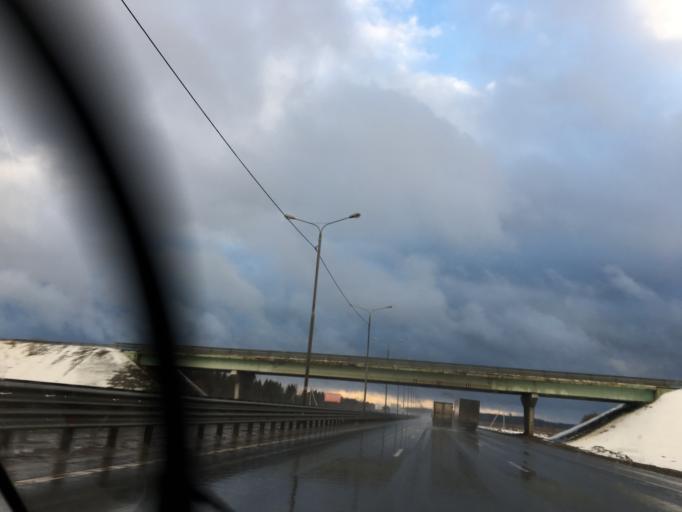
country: RU
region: Moskovskaya
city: Novyy Byt
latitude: 55.0595
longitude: 37.5635
